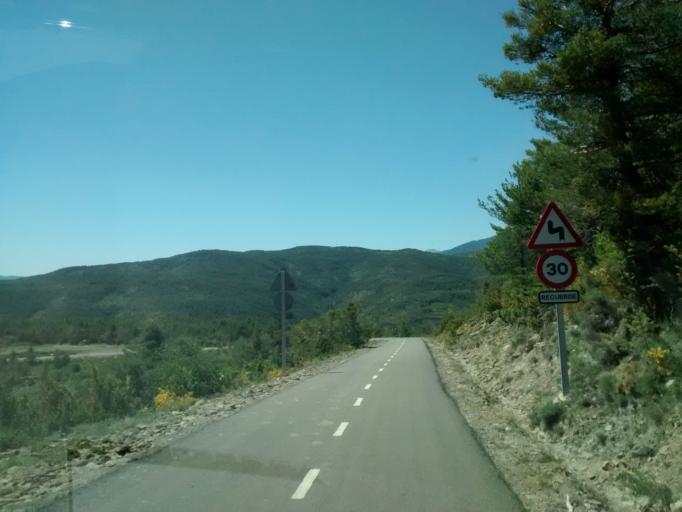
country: ES
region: Aragon
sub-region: Provincia de Huesca
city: Borau
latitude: 42.6739
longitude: -0.6116
